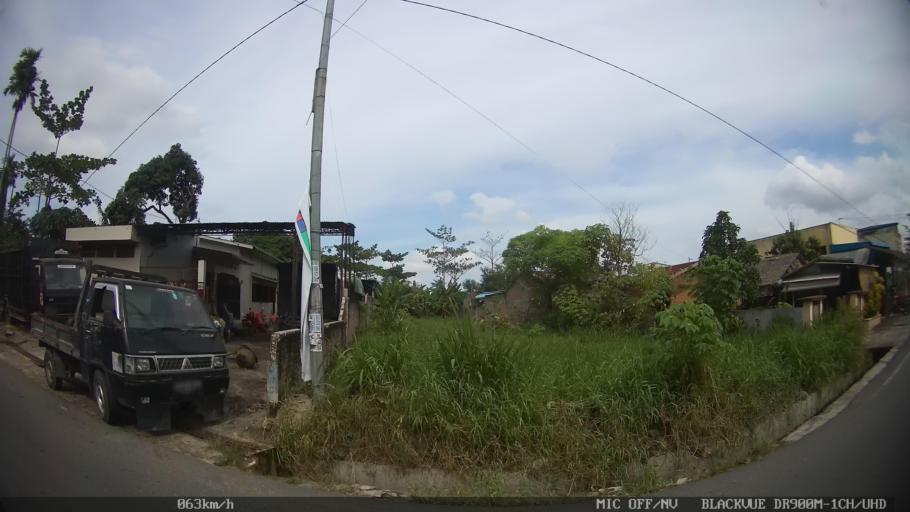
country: ID
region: North Sumatra
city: Percut
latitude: 3.5919
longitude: 98.8582
